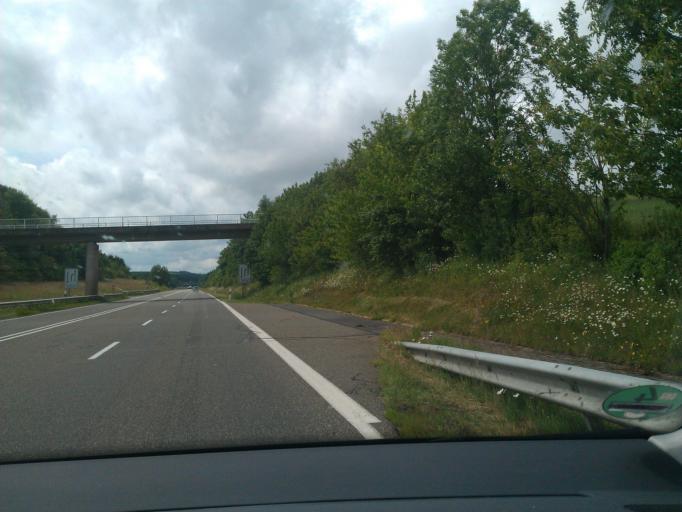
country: DE
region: Rheinland-Pfalz
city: Watzerath
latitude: 50.1996
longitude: 6.3626
